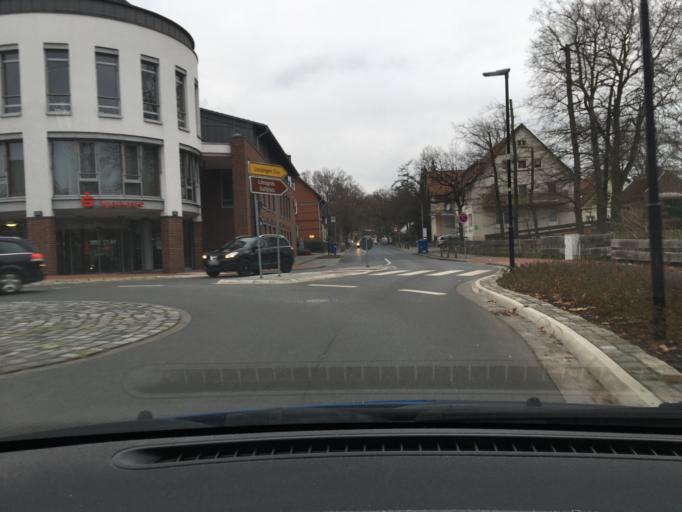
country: DE
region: Lower Saxony
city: Bad Fallingbostel
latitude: 52.8659
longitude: 9.6922
